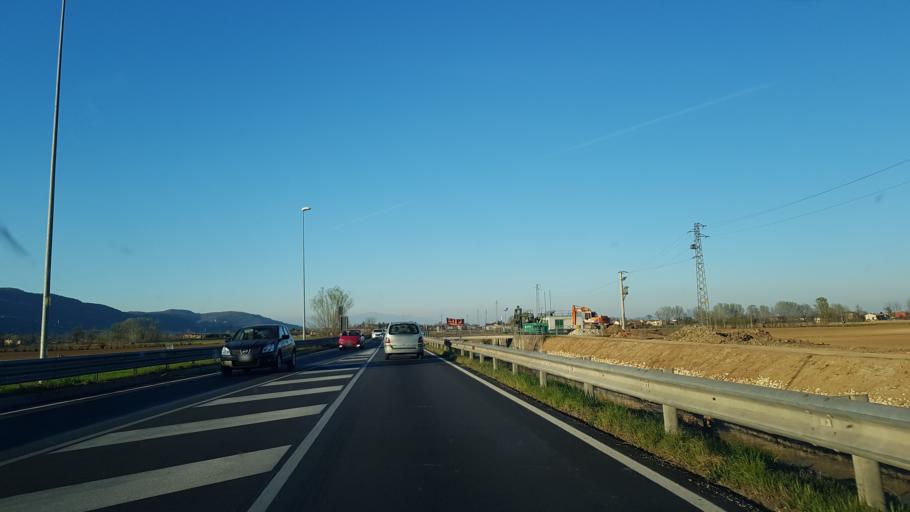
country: IT
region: Veneto
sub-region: Provincia di Vicenza
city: Ponte di Barbarano
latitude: 45.4000
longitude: 11.5796
